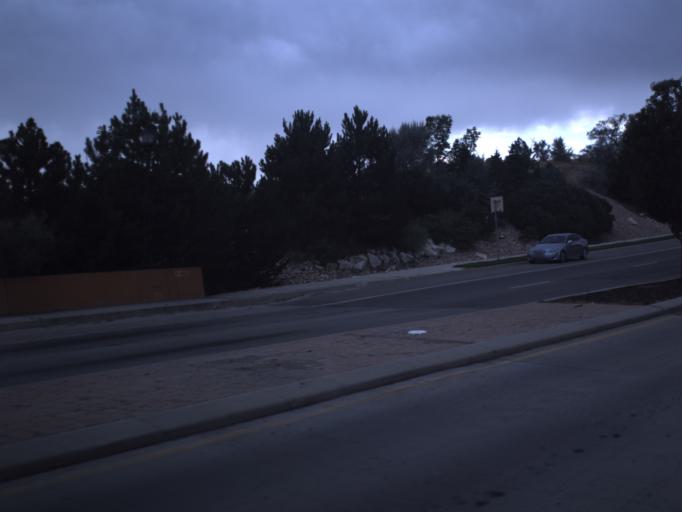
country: US
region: Utah
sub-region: Salt Lake County
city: Riverton
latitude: 40.5236
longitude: -111.9219
